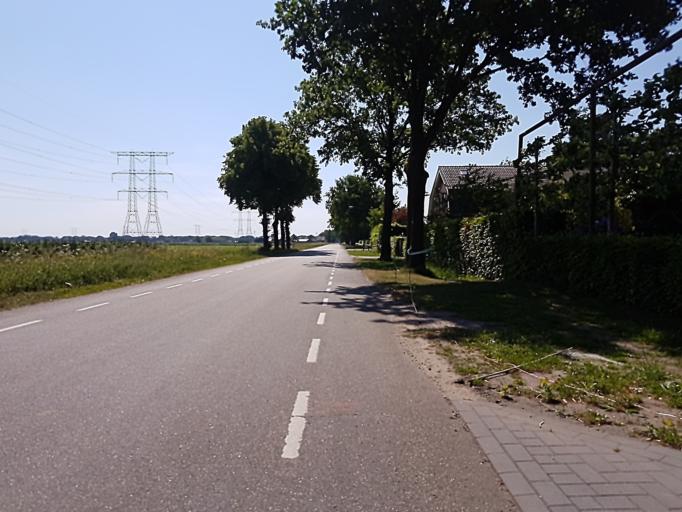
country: NL
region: North Brabant
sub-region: Gemeente Dongen
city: Dongen
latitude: 51.6350
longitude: 4.9944
